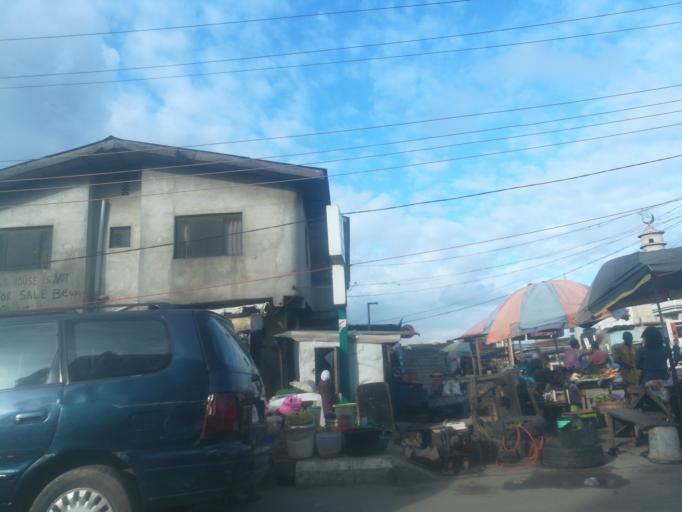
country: NG
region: Lagos
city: Somolu
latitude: 6.5389
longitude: 3.3851
